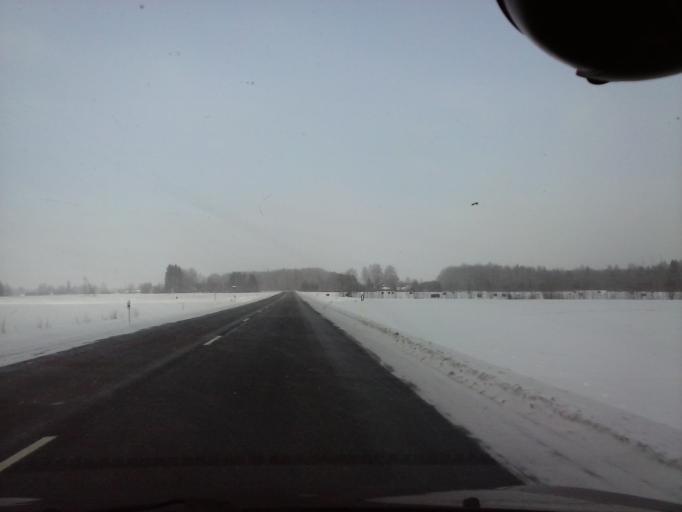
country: EE
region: Viljandimaa
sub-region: Abja vald
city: Abja-Paluoja
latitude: 58.2968
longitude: 25.2970
